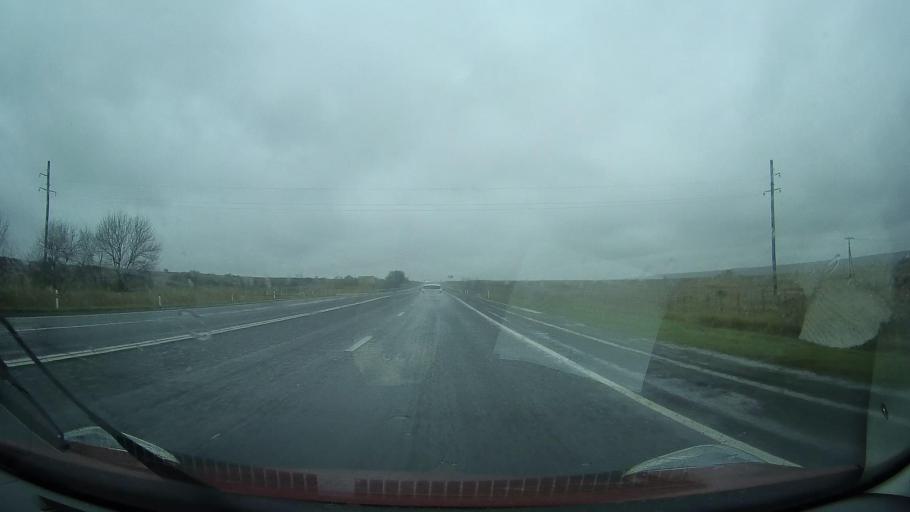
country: RU
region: Stavropol'skiy
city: Nevinnomyssk
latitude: 44.6230
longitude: 42.0734
